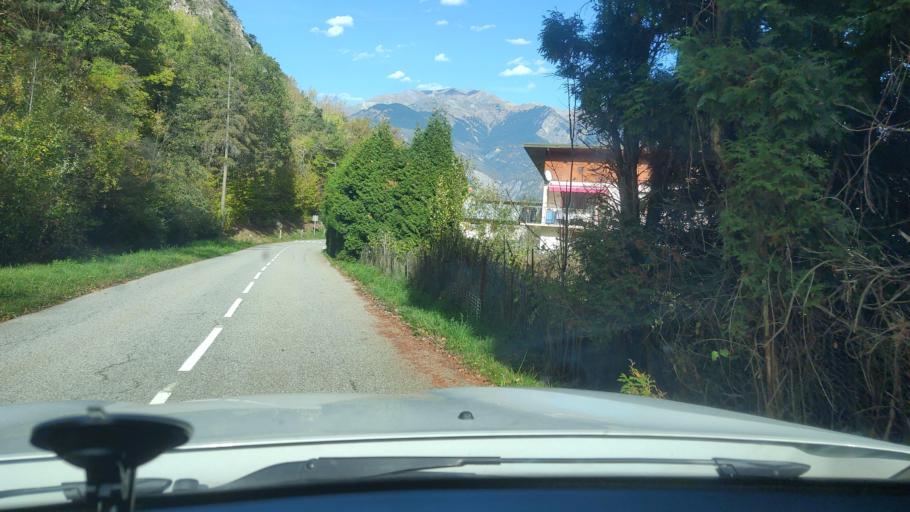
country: FR
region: Rhone-Alpes
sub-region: Departement de la Savoie
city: Saint-Jean-de-Maurienne
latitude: 45.2567
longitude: 6.3258
